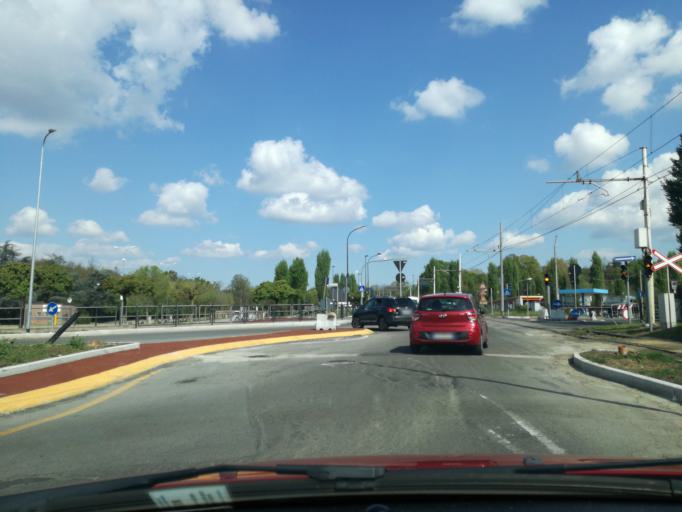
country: IT
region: Lombardy
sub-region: Provincia di Monza e Brianza
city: Limbiate
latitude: 45.6055
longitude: 9.1227
